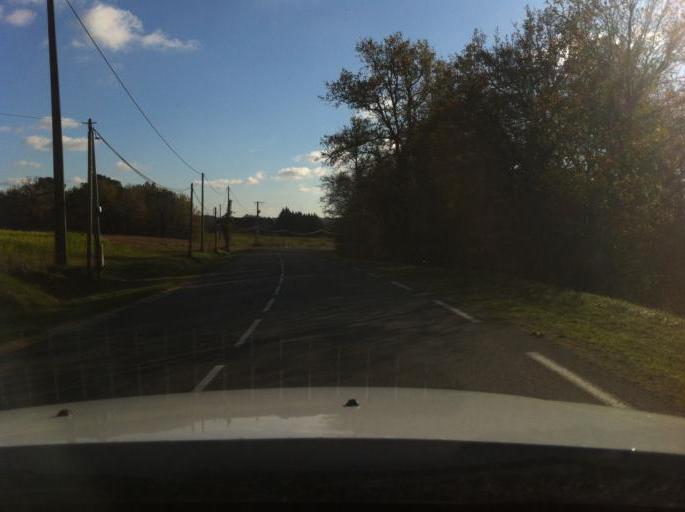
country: FR
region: Aquitaine
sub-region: Departement de la Dordogne
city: Rouffignac-Saint-Cernin-de-Reilhac
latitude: 45.0526
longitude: 0.8597
